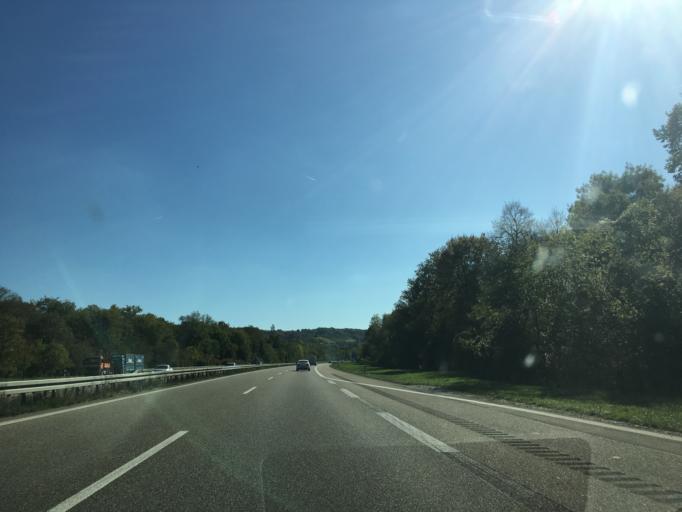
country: DE
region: Baden-Wuerttemberg
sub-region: Freiburg Region
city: Bad Bellingen
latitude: 47.7476
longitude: 7.5499
